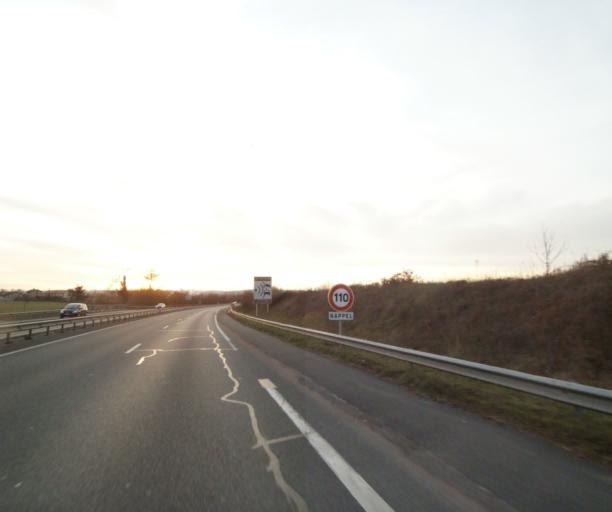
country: FR
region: Poitou-Charentes
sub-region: Departement de la Charente-Maritime
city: Les Gonds
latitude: 45.7315
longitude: -0.6163
